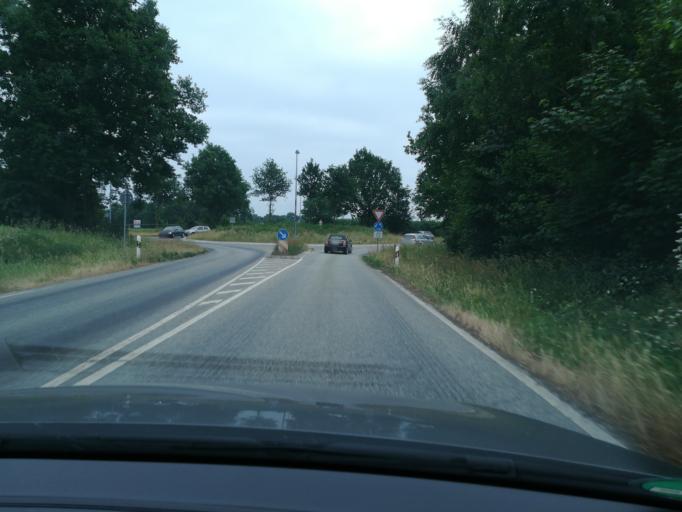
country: DE
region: Schleswig-Holstein
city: Siek
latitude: 53.6342
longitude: 10.3082
